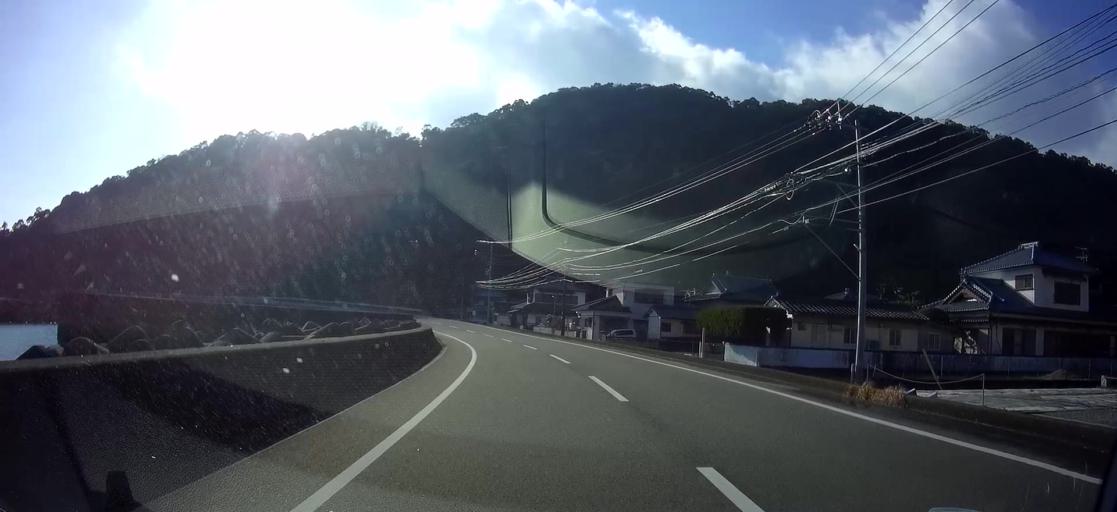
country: JP
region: Kumamoto
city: Minamata
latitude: 32.3874
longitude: 130.3830
